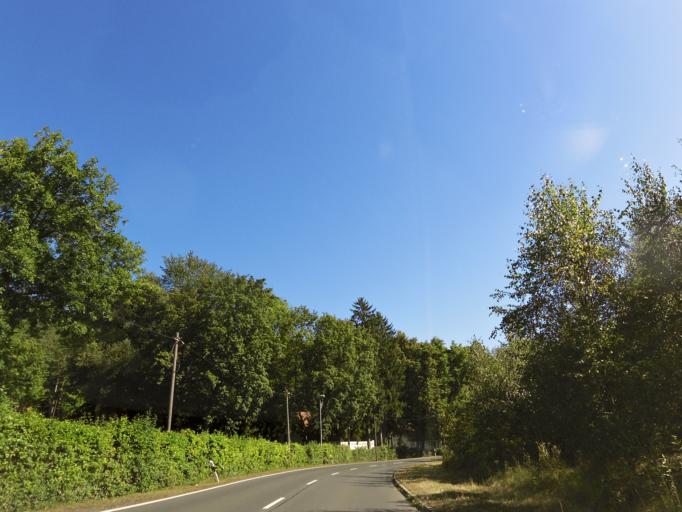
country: DE
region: Saxony
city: Dohna
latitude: 50.9441
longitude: 13.8655
